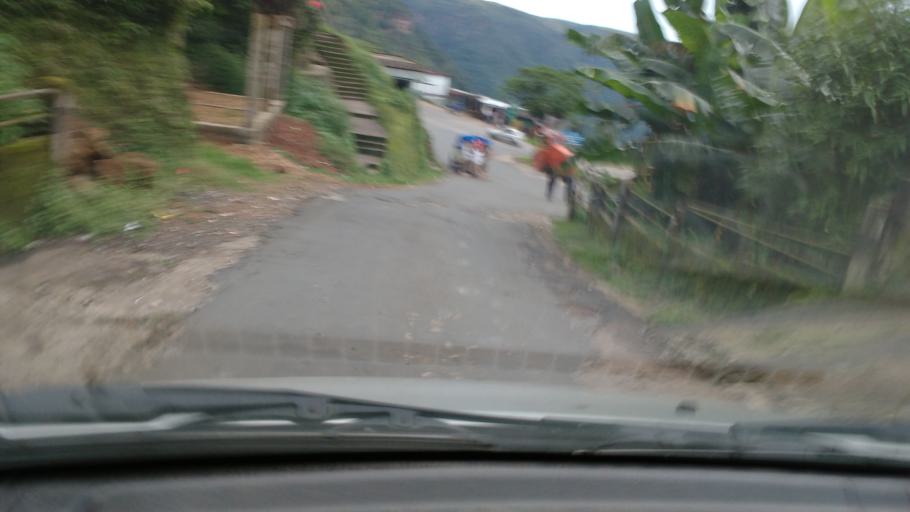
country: IN
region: Meghalaya
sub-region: East Khasi Hills
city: Cherrapunji
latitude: 25.2853
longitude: 91.7197
